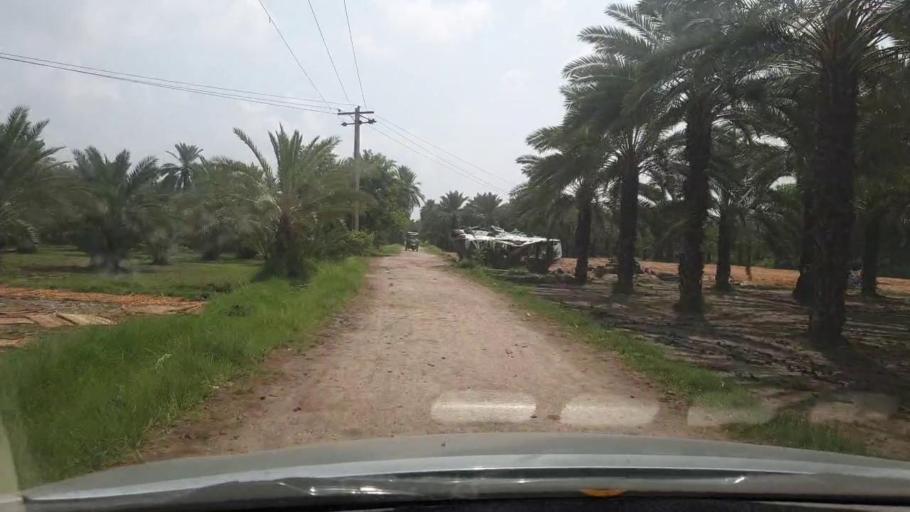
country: PK
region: Sindh
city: Khairpur
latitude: 27.5034
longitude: 68.7379
